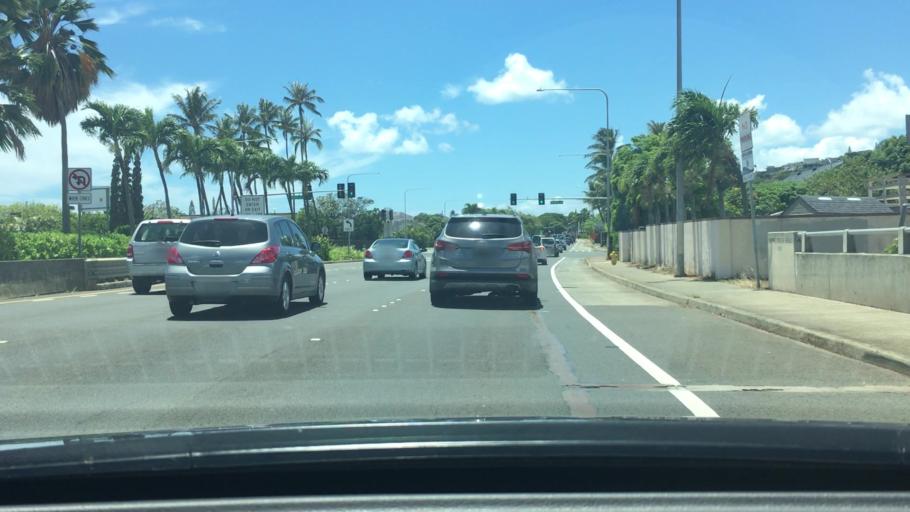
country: US
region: Hawaii
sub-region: Honolulu County
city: Waimanalo
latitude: 21.2785
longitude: -157.7509
